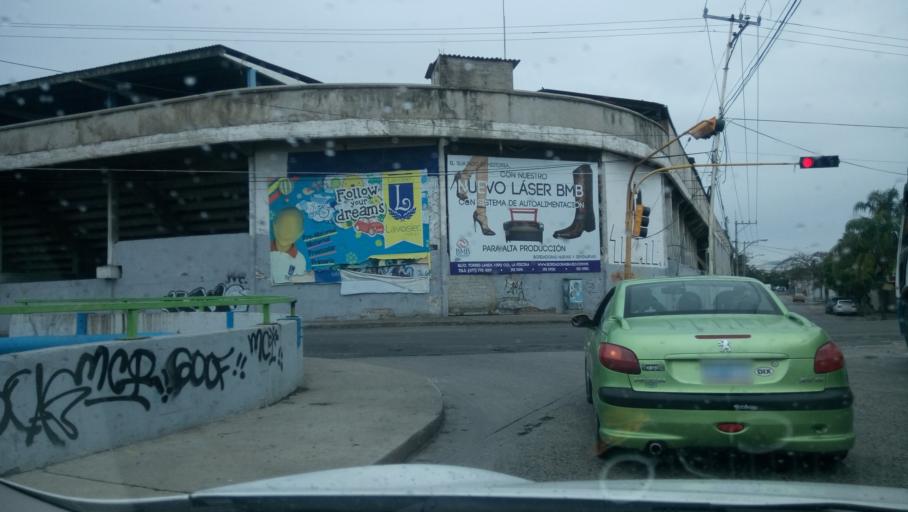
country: MX
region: Guanajuato
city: Leon
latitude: 21.1159
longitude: -101.6663
